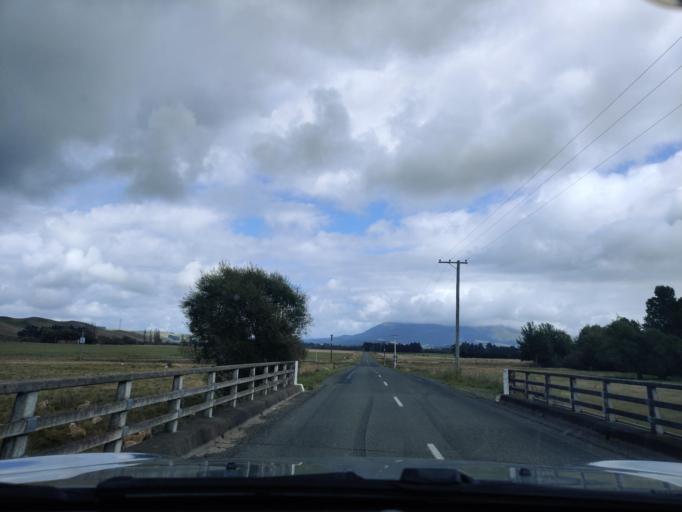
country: NZ
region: Canterbury
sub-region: Hurunui District
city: Amberley
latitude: -43.1274
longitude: 172.6834
